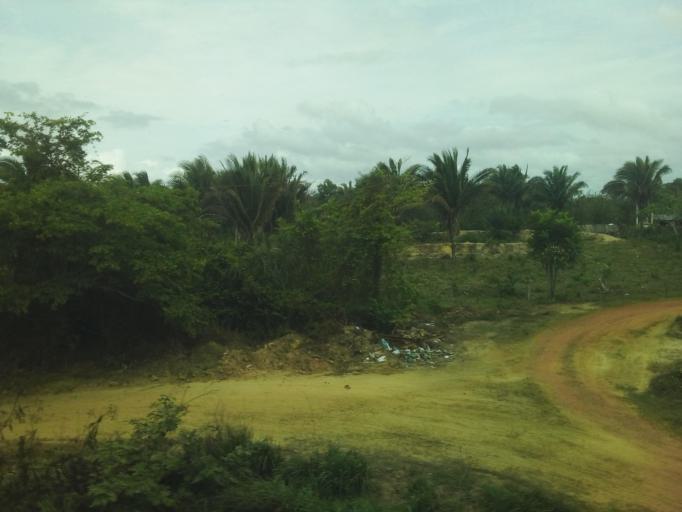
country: BR
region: Maranhao
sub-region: Itapecuru Mirim
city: Itapecuru Mirim
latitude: -3.3202
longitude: -44.4820
